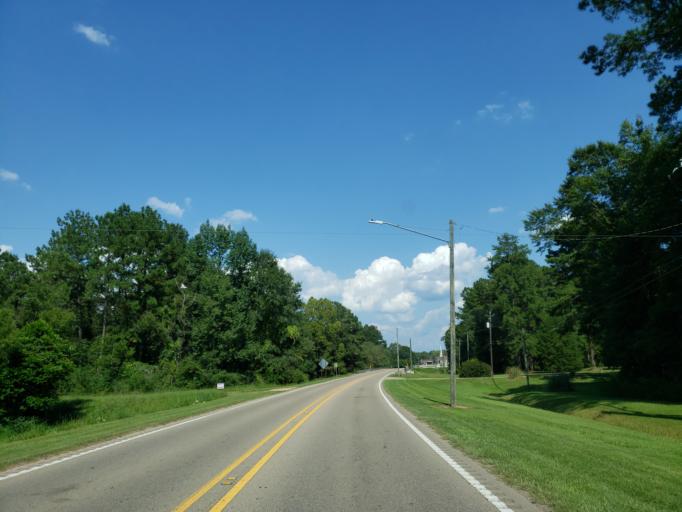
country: US
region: Mississippi
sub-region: Covington County
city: Collins
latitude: 31.5631
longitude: -89.5073
